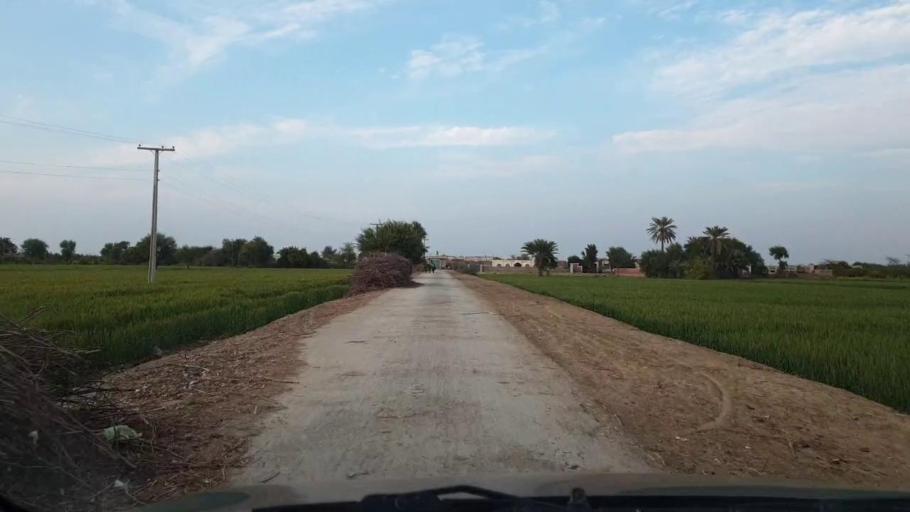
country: PK
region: Sindh
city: Jhol
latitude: 25.9865
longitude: 68.8656
